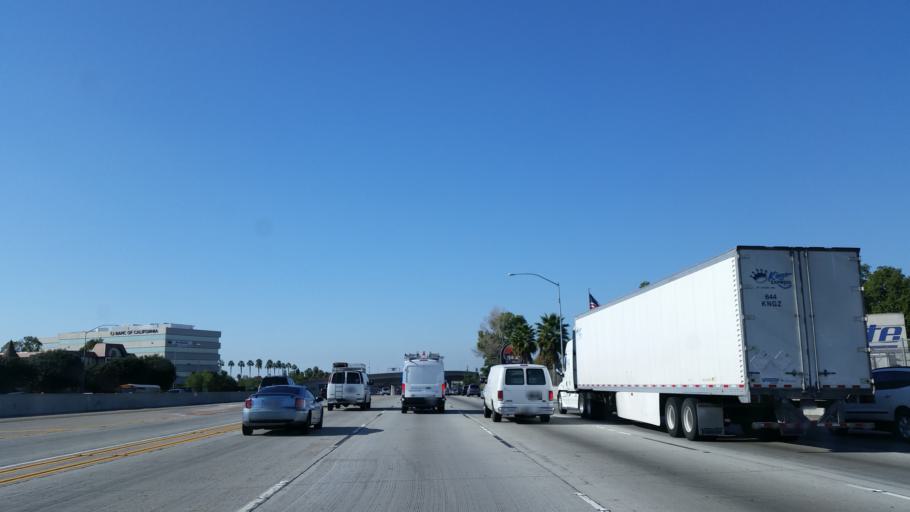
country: US
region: California
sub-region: Orange County
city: Anaheim
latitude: 33.8194
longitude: -117.9192
